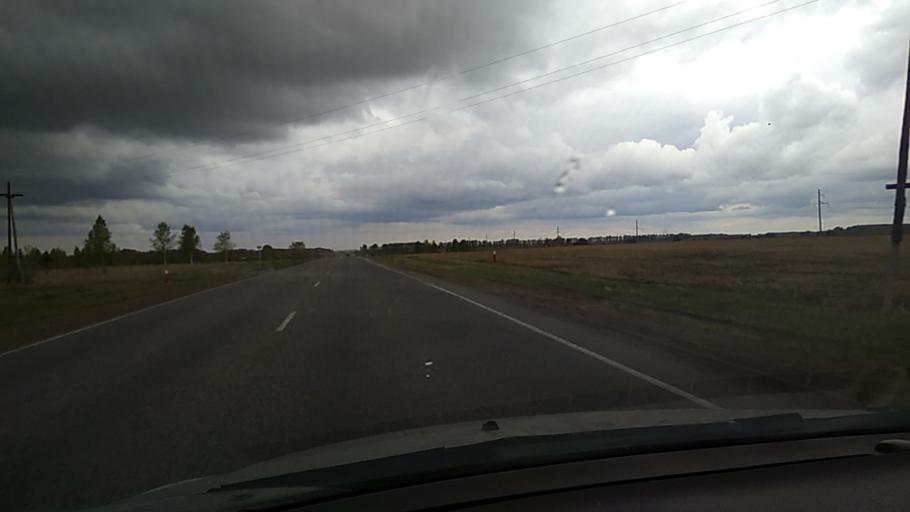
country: RU
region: Kurgan
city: Dalmatovo
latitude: 56.2897
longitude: 62.8513
